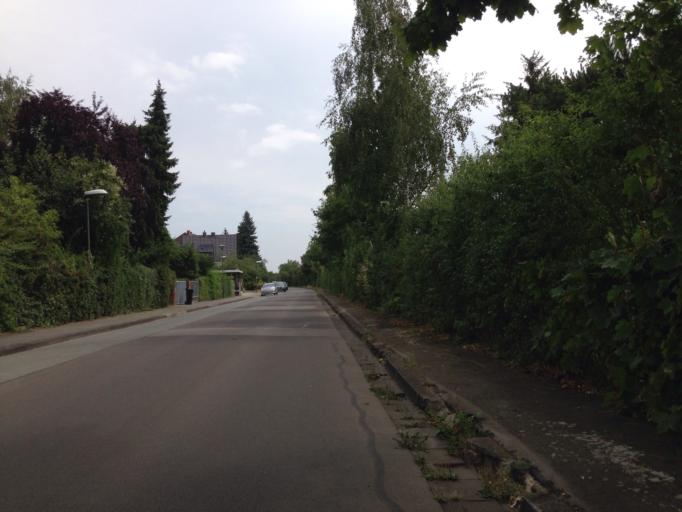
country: DE
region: Hesse
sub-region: Regierungsbezirk Giessen
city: Giessen
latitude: 50.5789
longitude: 8.6867
